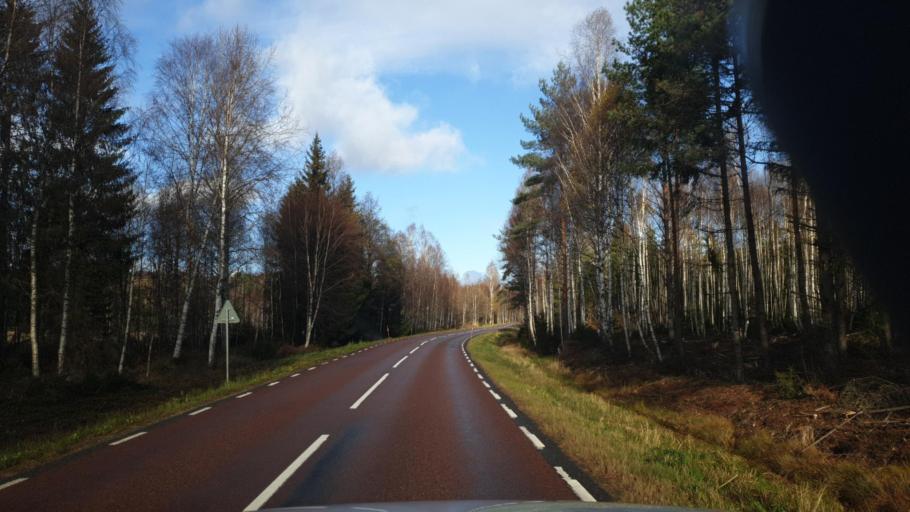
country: SE
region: Vaermland
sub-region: Grums Kommun
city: Grums
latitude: 59.4378
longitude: 12.9785
